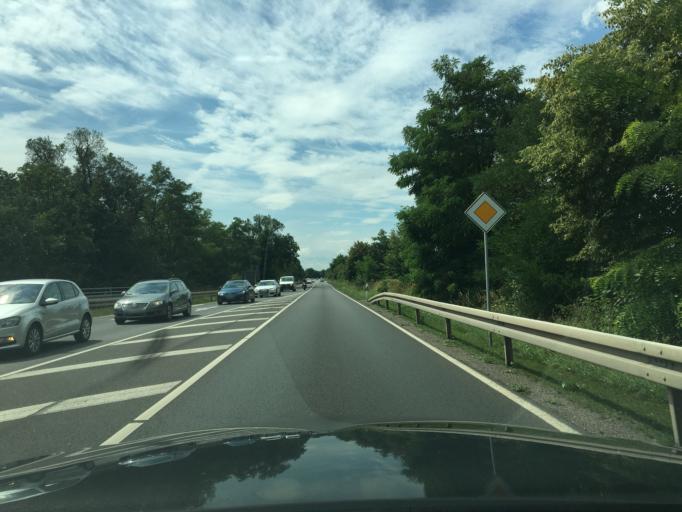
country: DE
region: Saxony-Anhalt
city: Zscherndorf
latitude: 51.5980
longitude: 12.2801
